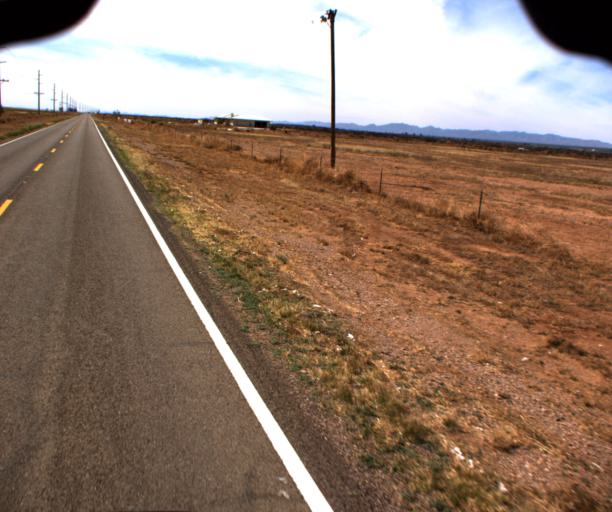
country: US
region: Arizona
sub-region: Cochise County
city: Tombstone
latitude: 31.7969
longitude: -109.6929
